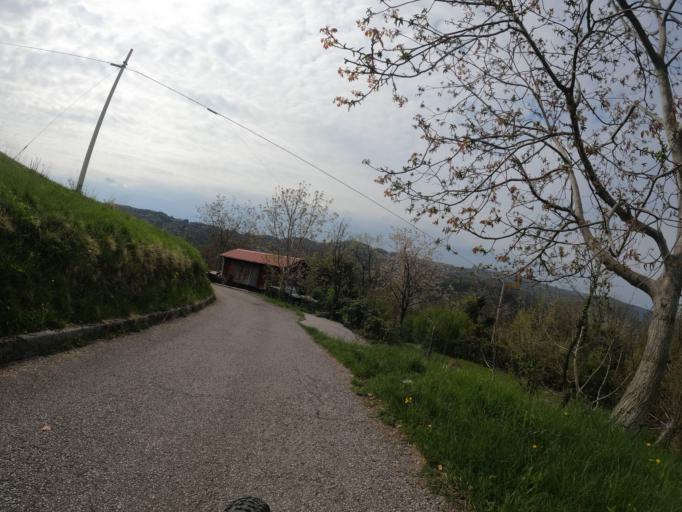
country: IT
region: Friuli Venezia Giulia
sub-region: Provincia di Udine
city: Stregna
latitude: 46.1371
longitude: 13.5899
